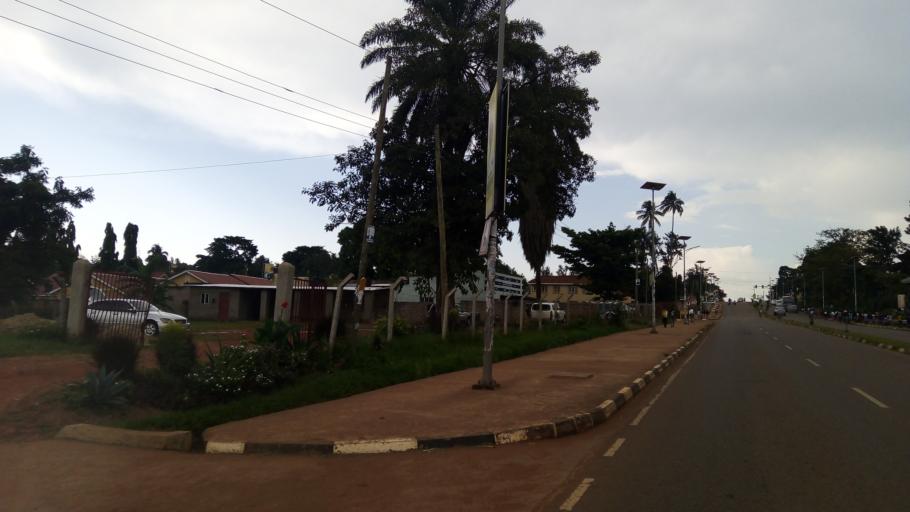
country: UG
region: Eastern Region
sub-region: Mbale District
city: Mbale
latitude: 1.0756
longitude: 34.1715
